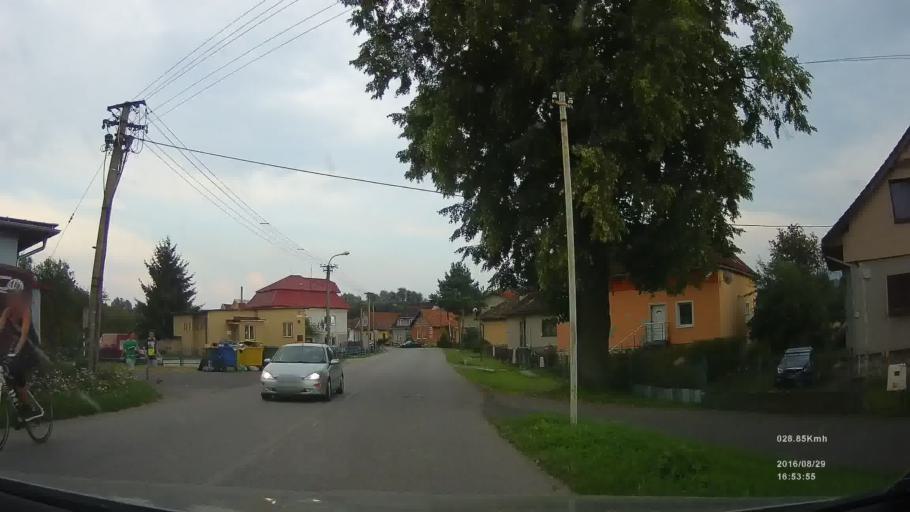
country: SK
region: Zilinsky
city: Ruzomberok
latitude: 49.0990
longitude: 19.4114
